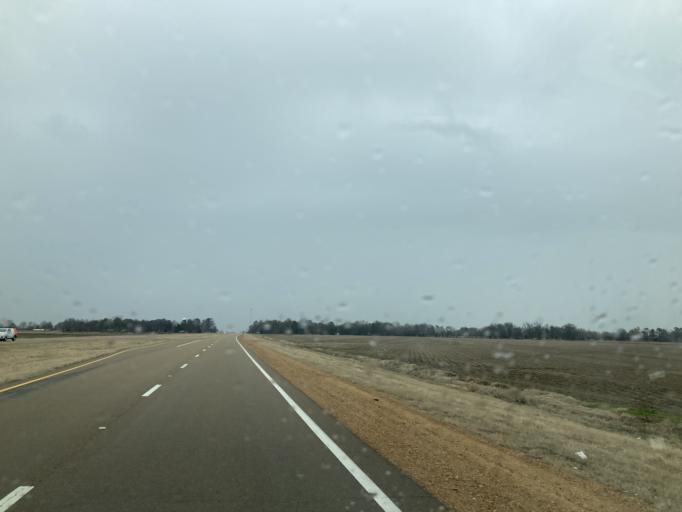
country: US
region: Mississippi
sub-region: Humphreys County
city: Belzoni
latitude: 33.0857
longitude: -90.4865
